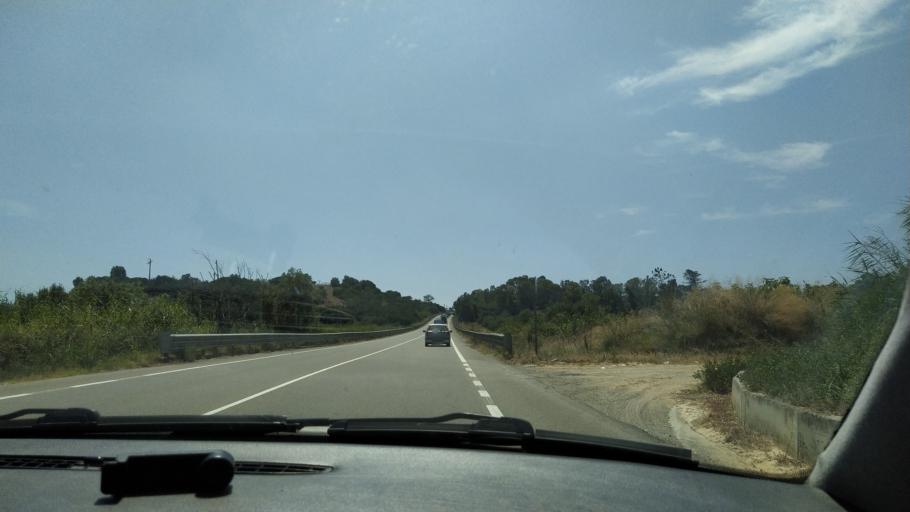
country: IT
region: Apulia
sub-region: Provincia di Taranto
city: Marina di Ginosa
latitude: 40.4306
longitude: 16.7937
